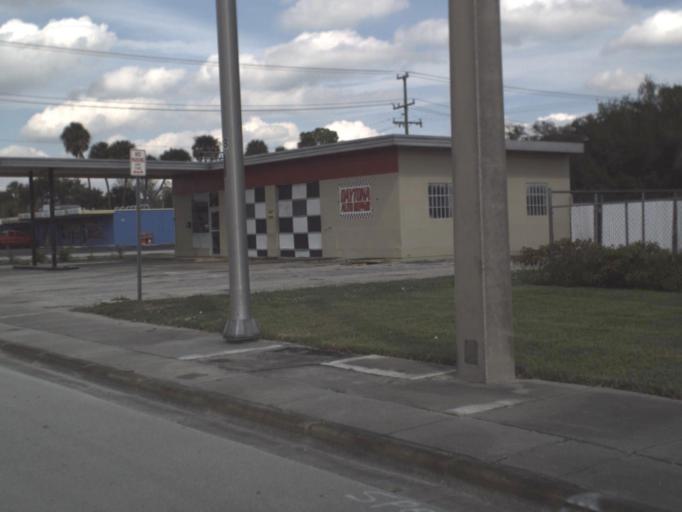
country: US
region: Florida
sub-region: Okeechobee County
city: Okeechobee
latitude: 27.2374
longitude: -80.8298
